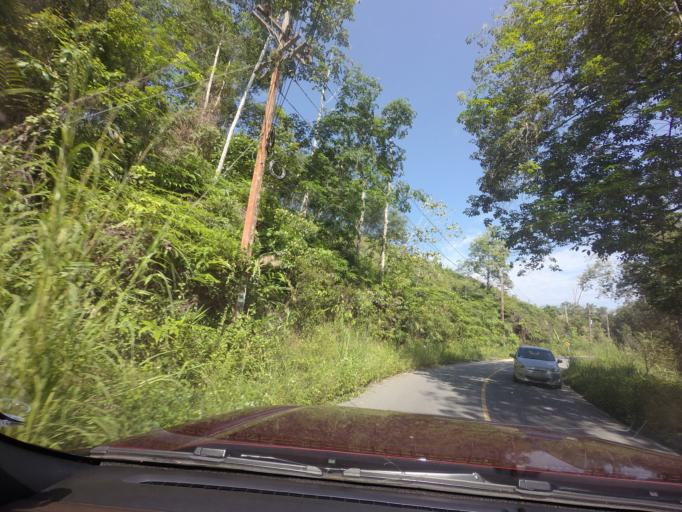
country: TH
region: Yala
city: Than To
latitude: 6.0077
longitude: 101.2233
